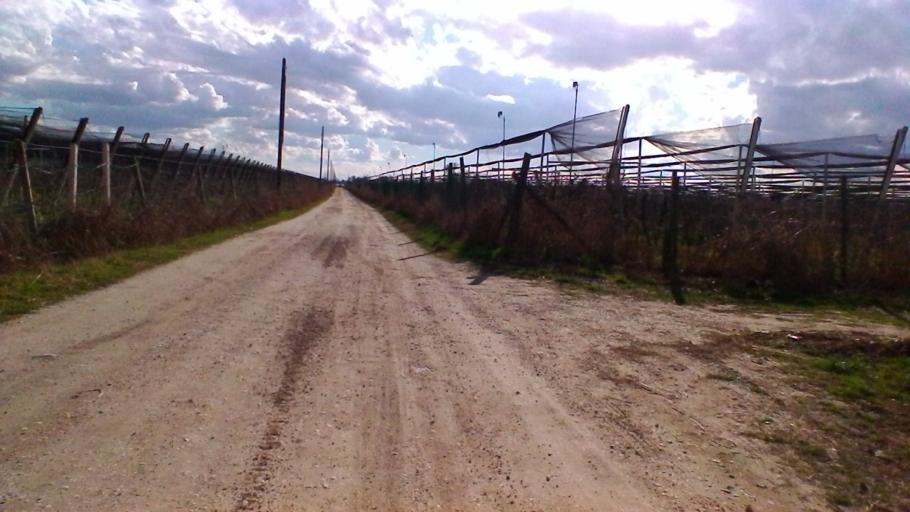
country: IT
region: Veneto
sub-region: Provincia di Verona
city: Povegliano Veronese
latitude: 45.3498
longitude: 10.9093
